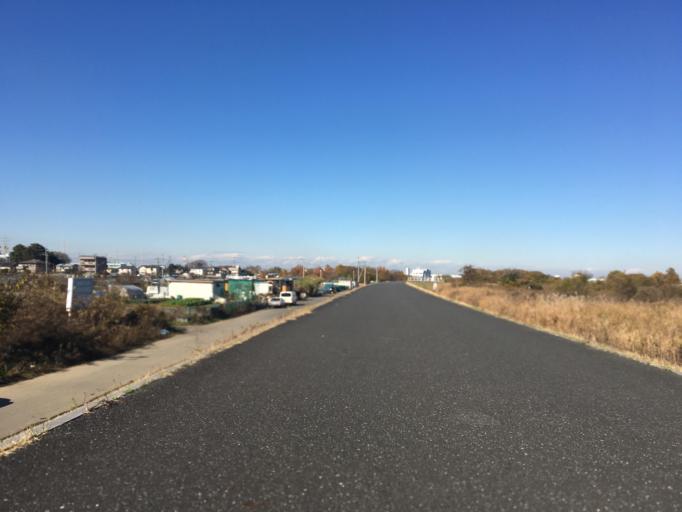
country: JP
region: Saitama
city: Yashio-shi
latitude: 35.8313
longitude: 139.8437
